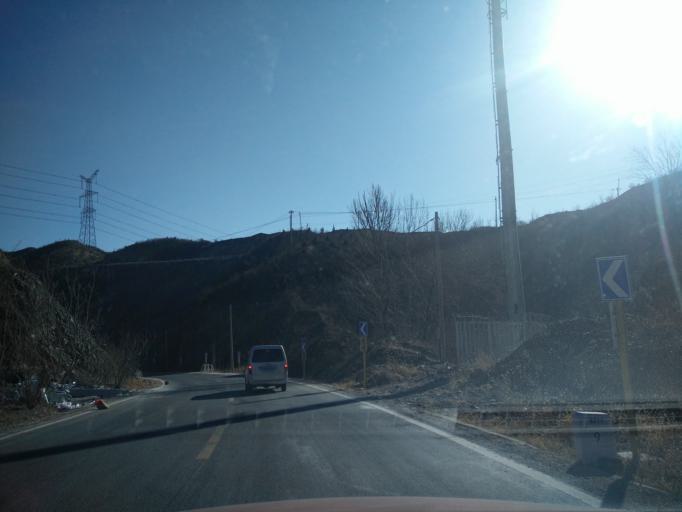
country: CN
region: Beijing
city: Zhaitang
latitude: 40.0303
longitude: 115.7068
